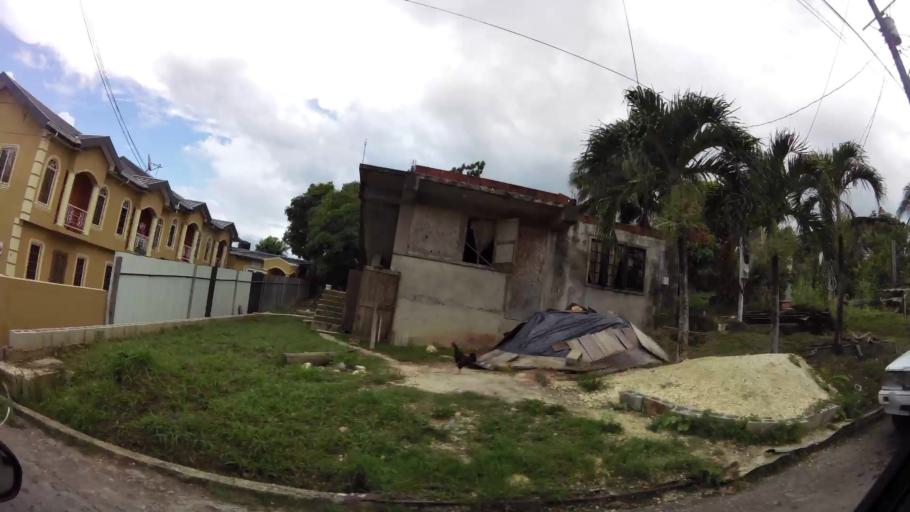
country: TT
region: City of San Fernando
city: Mon Repos
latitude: 10.2697
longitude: -61.4513
